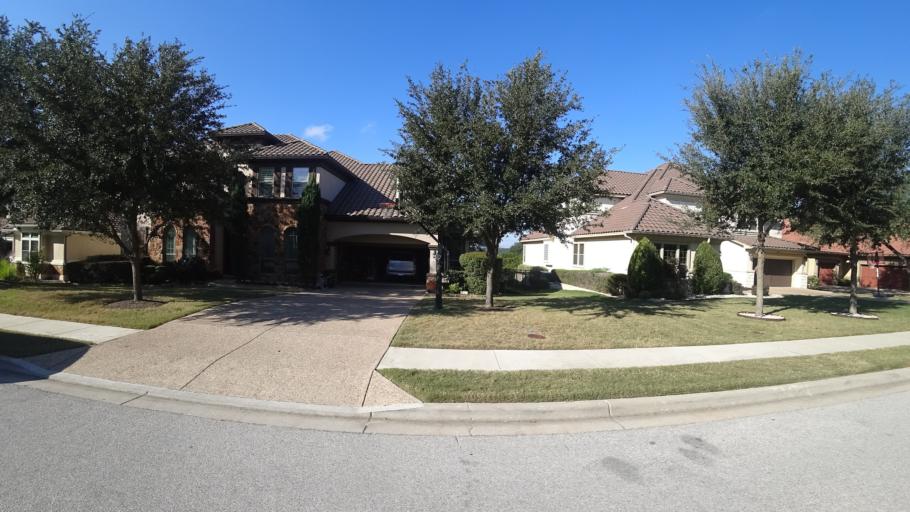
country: US
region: Texas
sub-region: Travis County
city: Bee Cave
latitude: 30.3472
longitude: -97.8940
